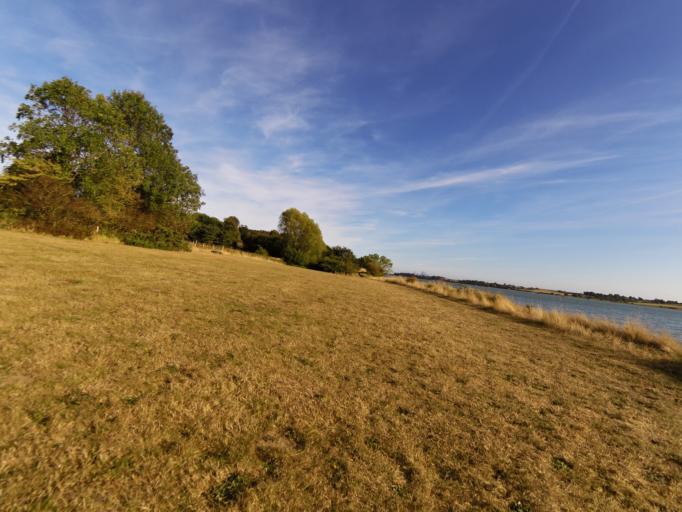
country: GB
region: England
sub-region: Suffolk
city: Kesgrave
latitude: 52.0054
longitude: 1.2333
